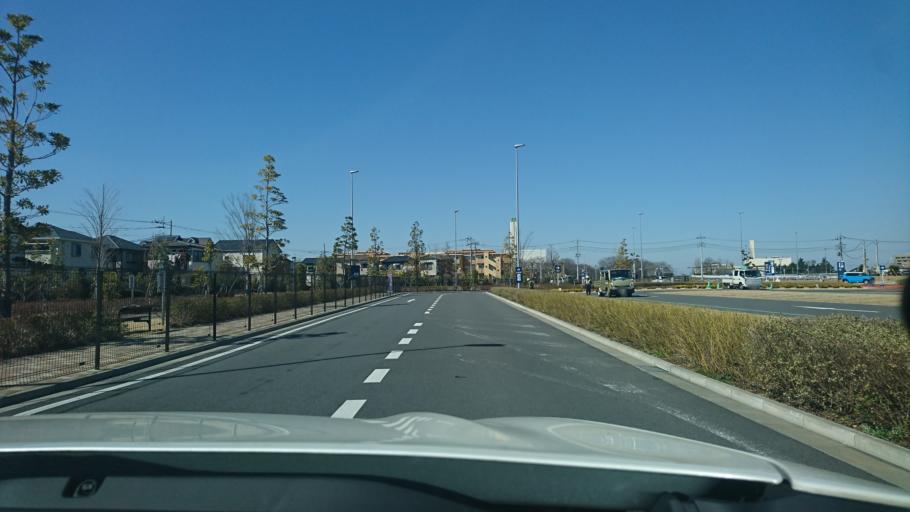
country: JP
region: Saitama
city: Oi
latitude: 35.8622
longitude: 139.5464
